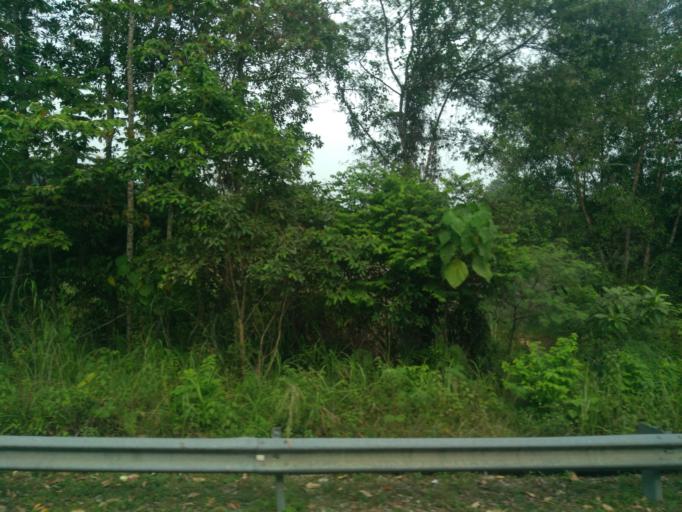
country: MY
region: Perak
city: Ipoh
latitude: 4.5538
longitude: 101.1657
